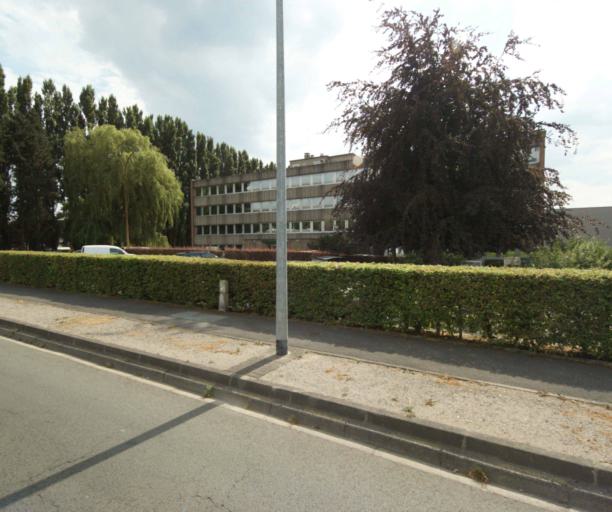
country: FR
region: Nord-Pas-de-Calais
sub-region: Departement du Nord
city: Neuville-en-Ferrain
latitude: 50.7562
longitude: 3.1635
